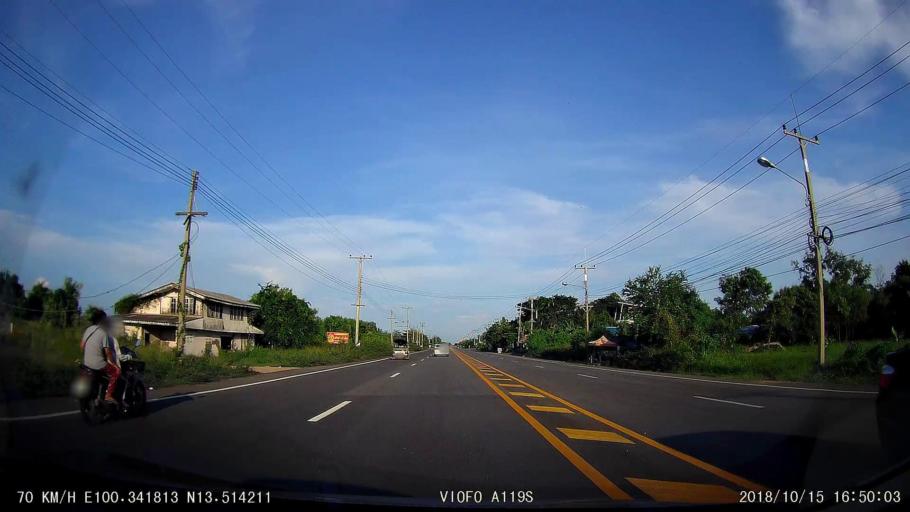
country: TH
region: Samut Sakhon
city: Samut Sakhon
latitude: 13.5142
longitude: 100.3419
